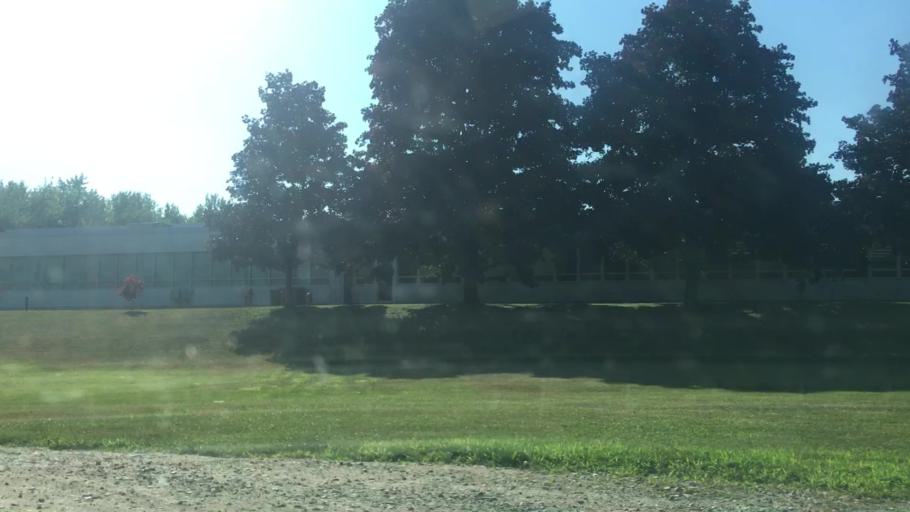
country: US
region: Maine
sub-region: York County
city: Buxton
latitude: 43.7482
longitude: -70.5386
